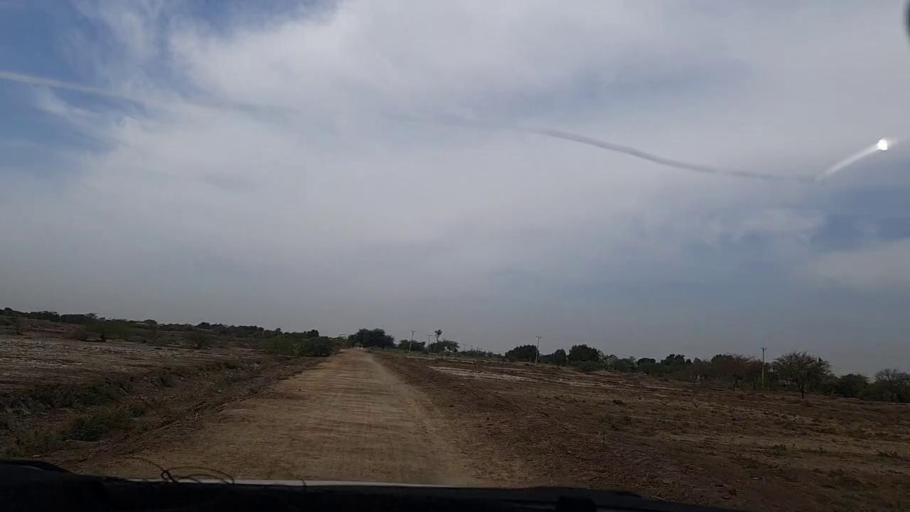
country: PK
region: Sindh
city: Dhoro Naro
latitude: 25.4506
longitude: 69.4886
